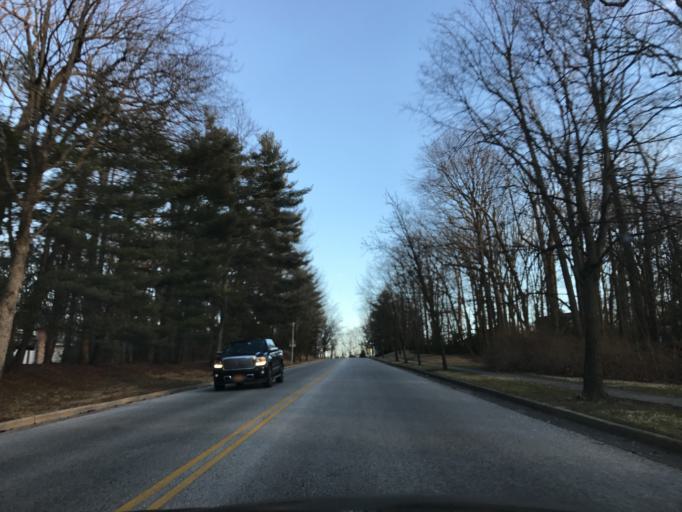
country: US
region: Maryland
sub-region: Harford County
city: Edgewood
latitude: 39.4051
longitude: -76.3432
